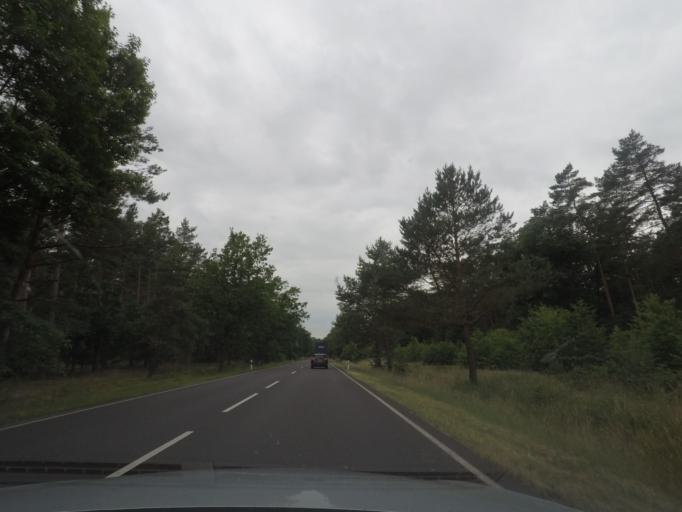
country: DE
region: Saxony-Anhalt
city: Haldensleben I
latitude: 52.3271
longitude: 11.4423
